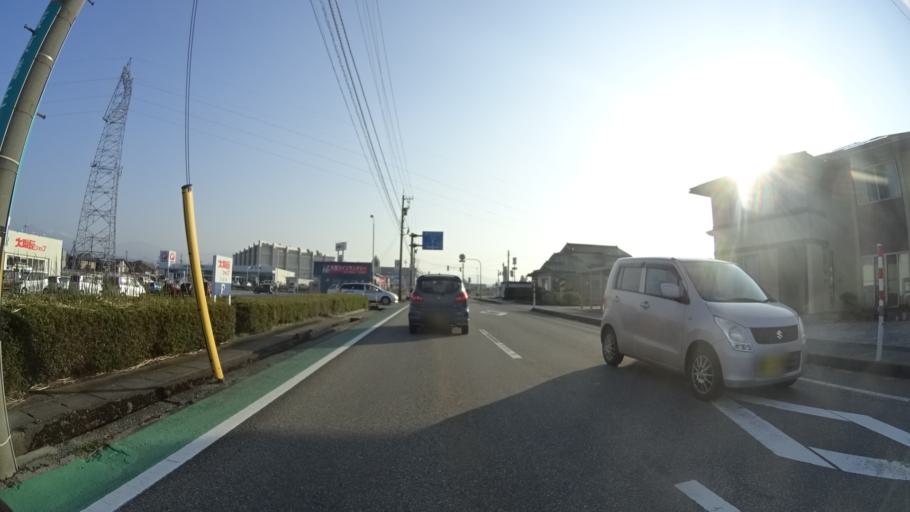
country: JP
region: Toyama
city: Kamiichi
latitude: 36.6500
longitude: 137.3135
